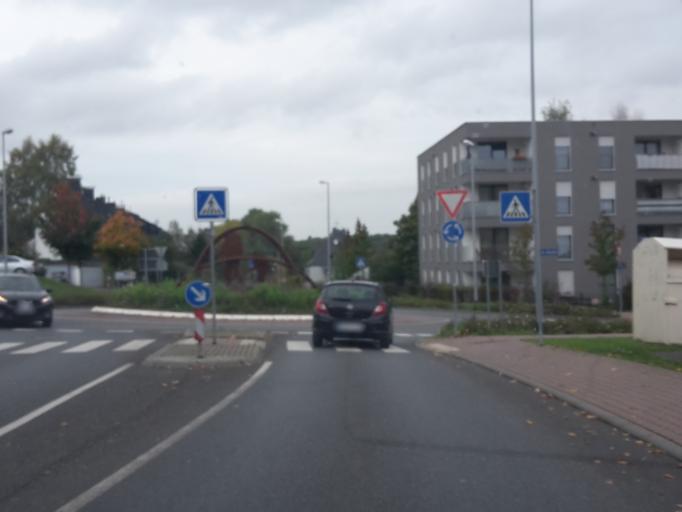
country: DE
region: Hesse
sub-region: Regierungsbezirk Darmstadt
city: Idstein
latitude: 50.2269
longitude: 8.2649
